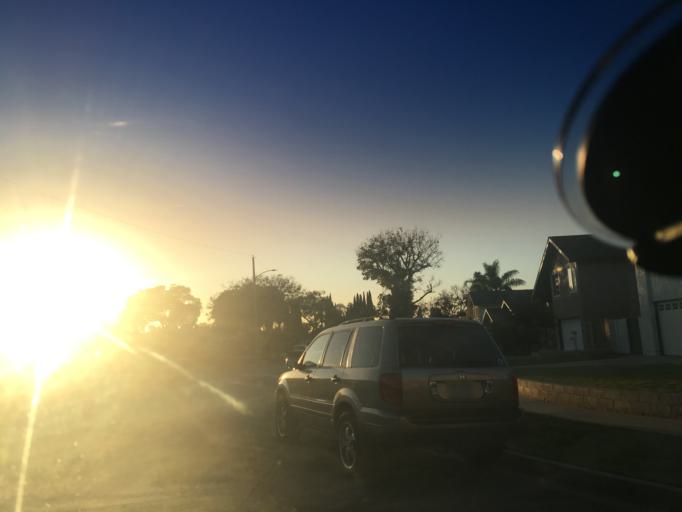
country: US
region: California
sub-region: Orange County
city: Anaheim
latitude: 33.8236
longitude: -117.8874
